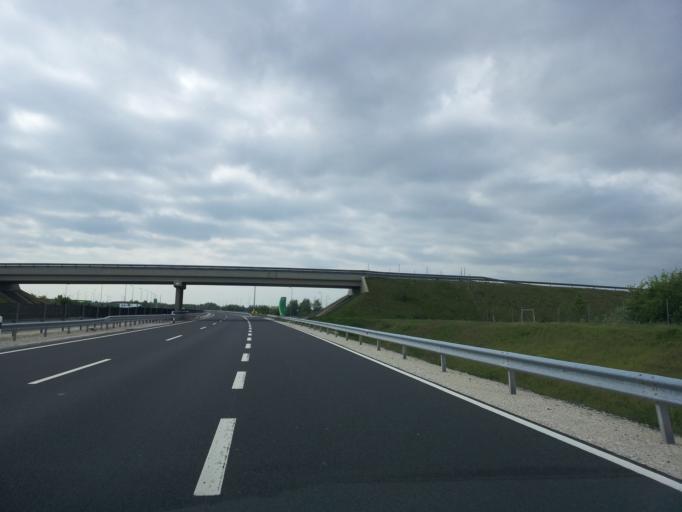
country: HU
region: Tolna
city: Szedres
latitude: 46.4427
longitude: 18.7075
